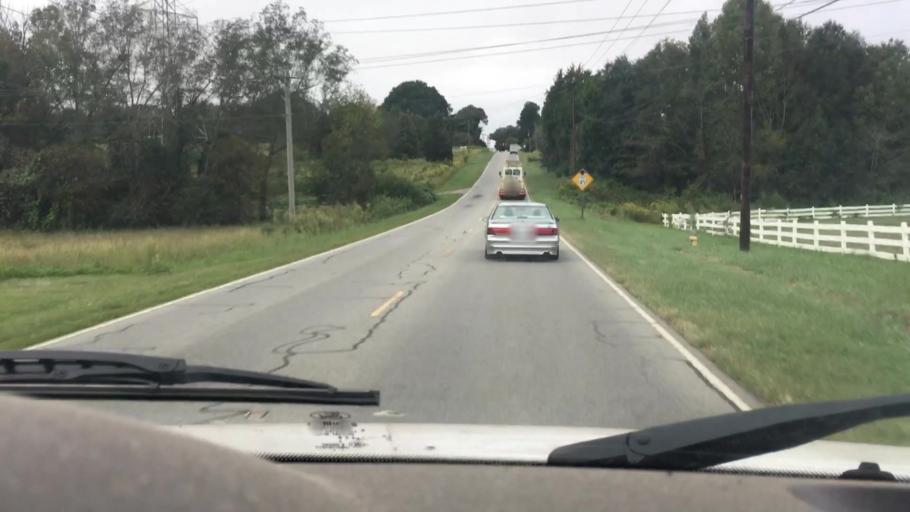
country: US
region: North Carolina
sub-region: Catawba County
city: Lake Norman of Catawba
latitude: 35.5916
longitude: -80.9712
